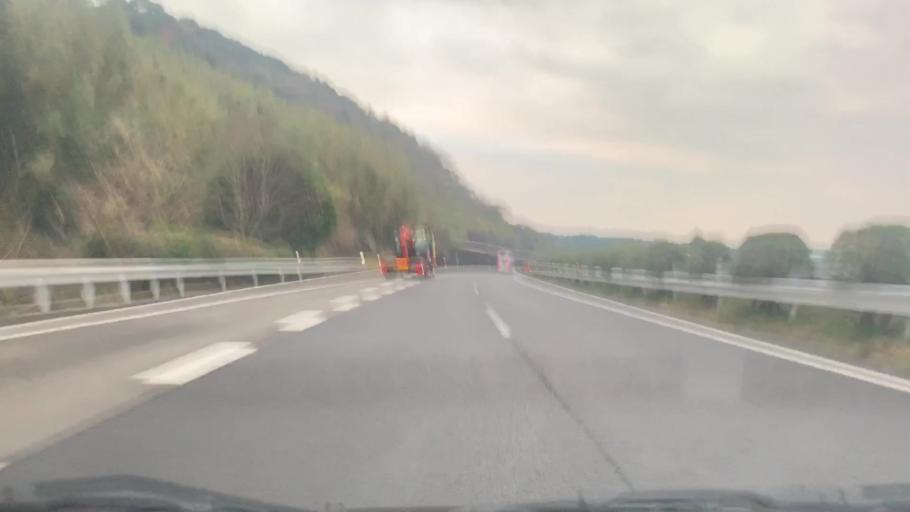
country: JP
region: Nagasaki
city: Omura
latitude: 32.9880
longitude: 129.9584
